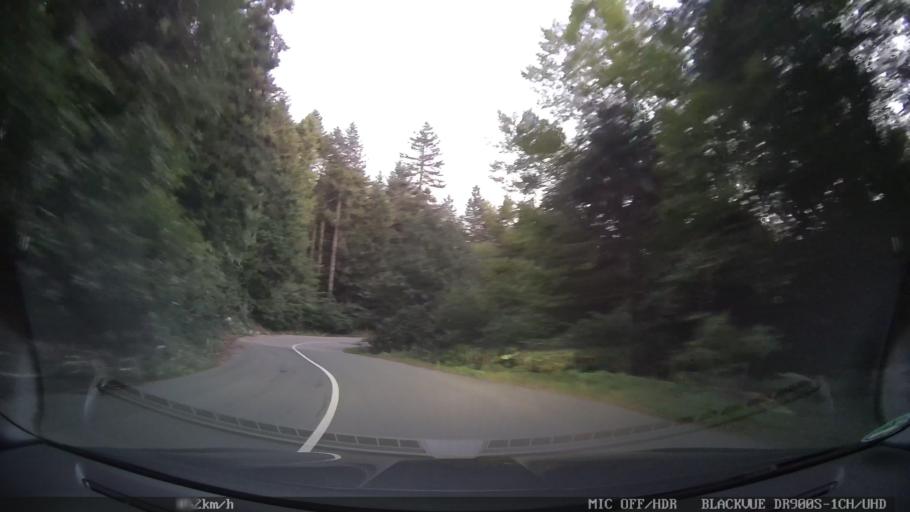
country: HR
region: Primorsko-Goranska
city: Novi Vinodolski
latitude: 45.1934
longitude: 14.8806
